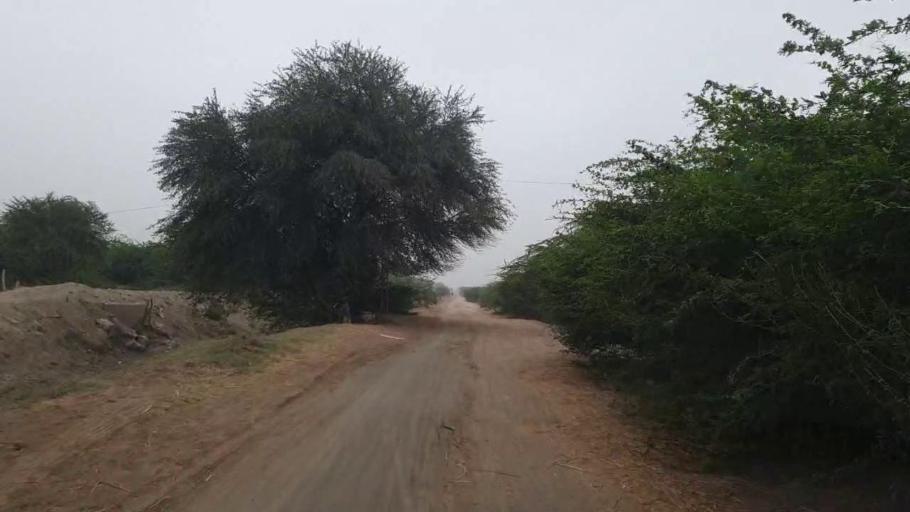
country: PK
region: Sindh
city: Badin
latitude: 24.6105
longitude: 68.6777
